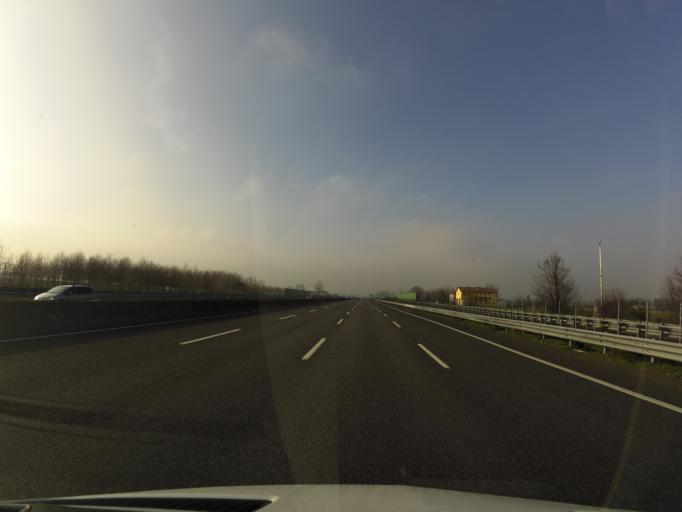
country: IT
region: Emilia-Romagna
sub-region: Provincia di Modena
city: Montale
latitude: 44.6022
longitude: 10.9231
